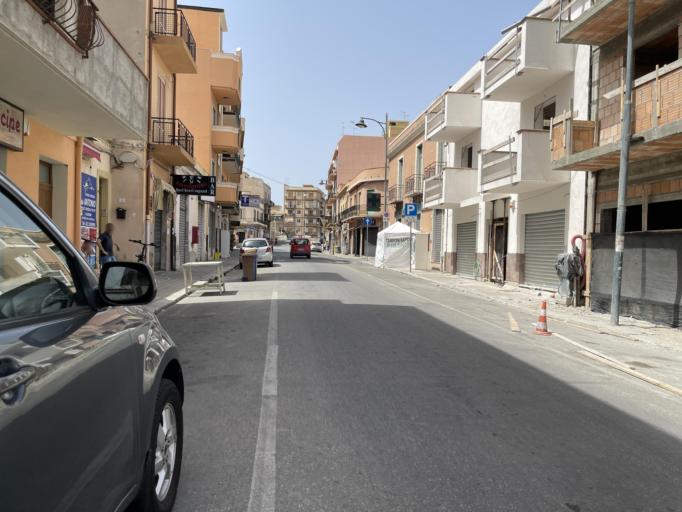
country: IT
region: Calabria
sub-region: Provincia di Reggio Calabria
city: Reggio Calabria
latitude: 38.1001
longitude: 15.6425
